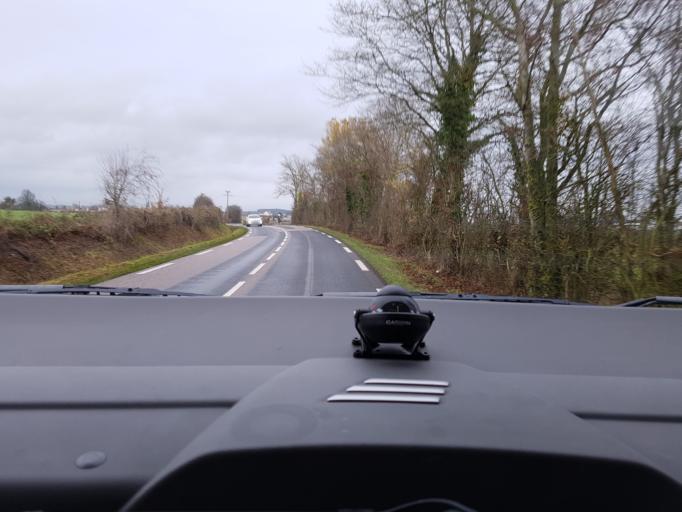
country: FR
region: Haute-Normandie
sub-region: Departement de la Seine-Maritime
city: Gournay-en-Bray
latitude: 49.4703
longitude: 1.7081
